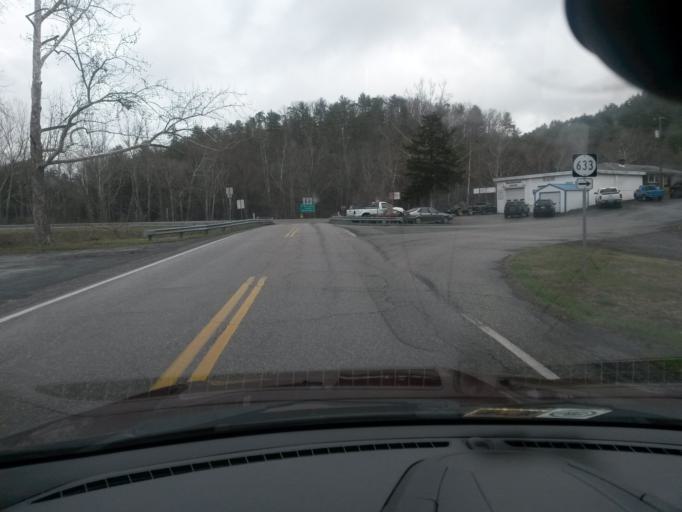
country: US
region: Virginia
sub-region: Bath County
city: Warm Springs
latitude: 37.9957
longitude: -79.6232
